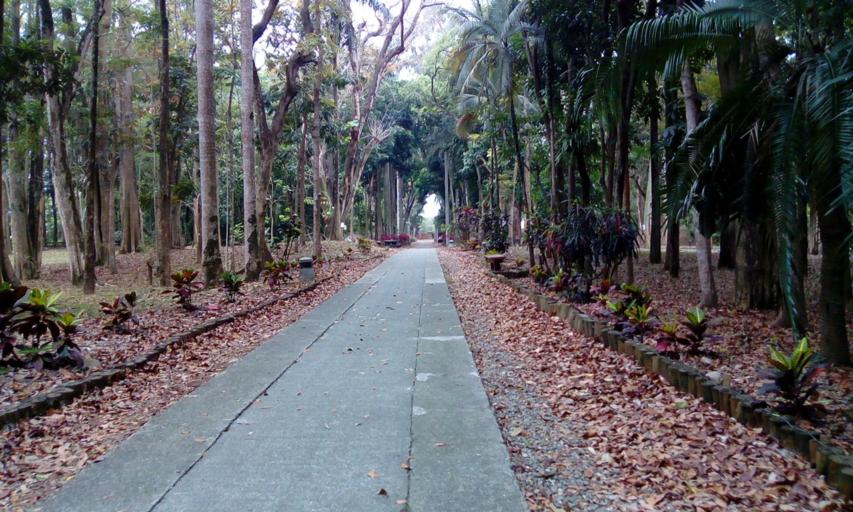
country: TW
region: Taiwan
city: Lugu
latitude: 23.7752
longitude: 120.6728
